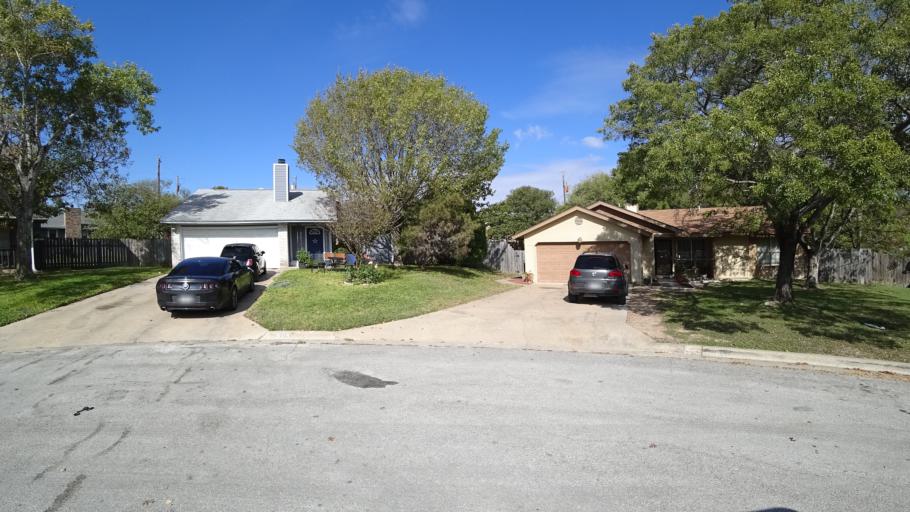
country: US
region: Texas
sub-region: Travis County
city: Windemere
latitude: 30.4524
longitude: -97.6445
